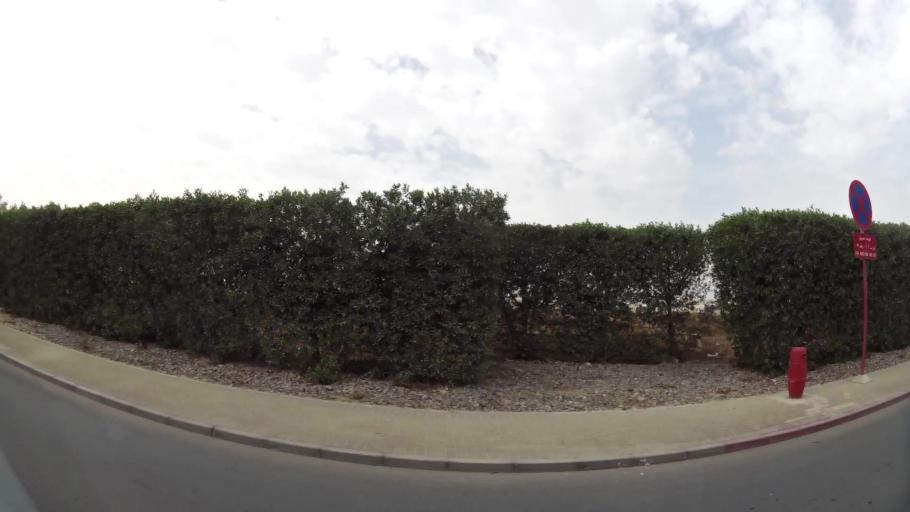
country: AE
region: Abu Dhabi
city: Abu Dhabi
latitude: 24.3105
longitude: 54.6182
